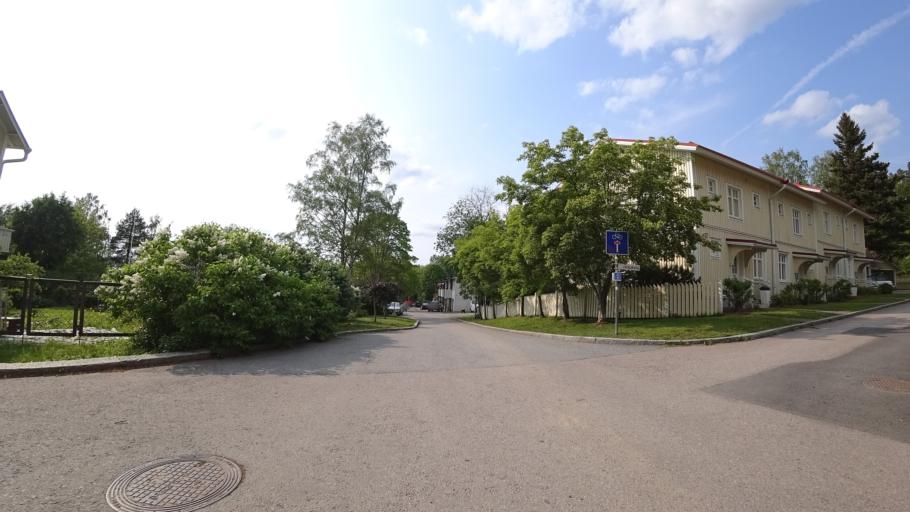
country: FI
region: Pirkanmaa
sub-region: Tampere
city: Tampere
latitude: 61.4999
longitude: 23.7127
